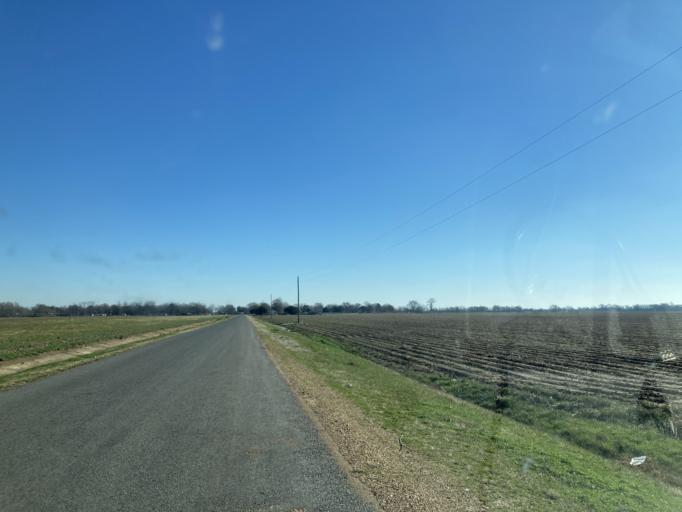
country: US
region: Mississippi
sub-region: Yazoo County
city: Yazoo City
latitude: 32.9775
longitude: -90.6048
